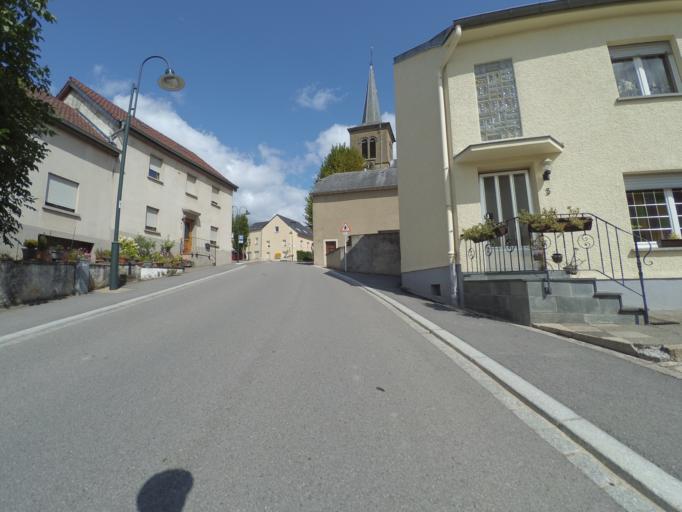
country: LU
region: Grevenmacher
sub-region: Canton de Remich
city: Lenningen
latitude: 49.6218
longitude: 6.3539
